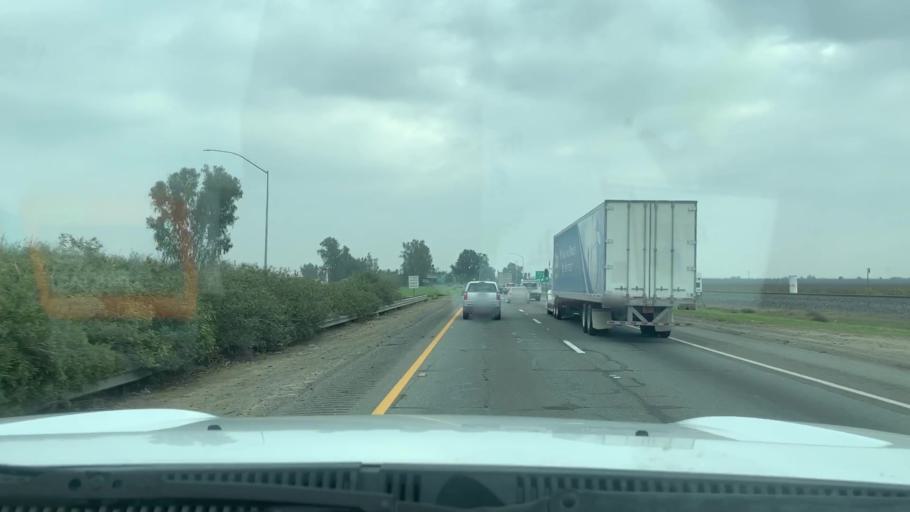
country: US
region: California
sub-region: Tulare County
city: Tulare
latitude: 36.2612
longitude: -119.3611
